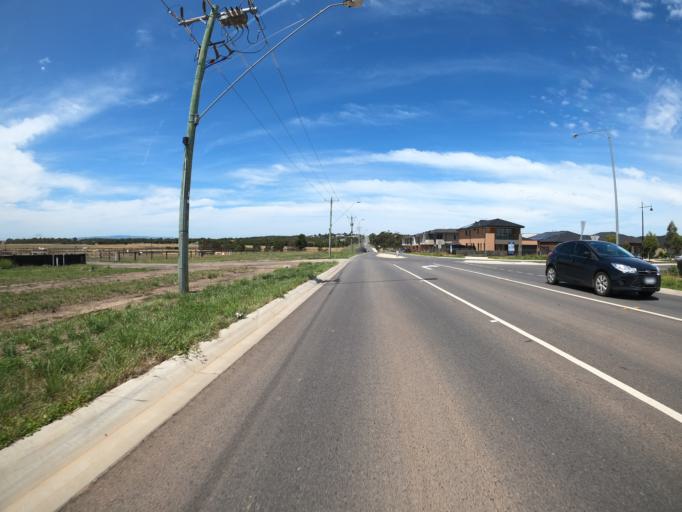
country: AU
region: Victoria
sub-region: Hume
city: Craigieburn
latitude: -37.5660
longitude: 144.9098
